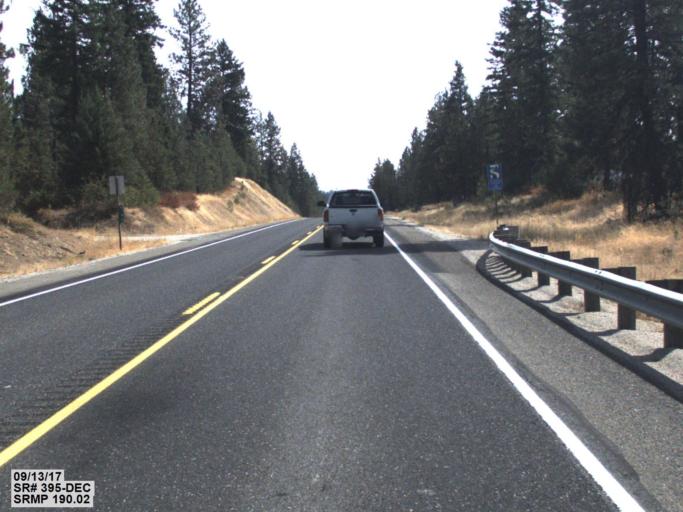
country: US
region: Washington
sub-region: Spokane County
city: Deer Park
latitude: 48.0529
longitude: -117.6147
